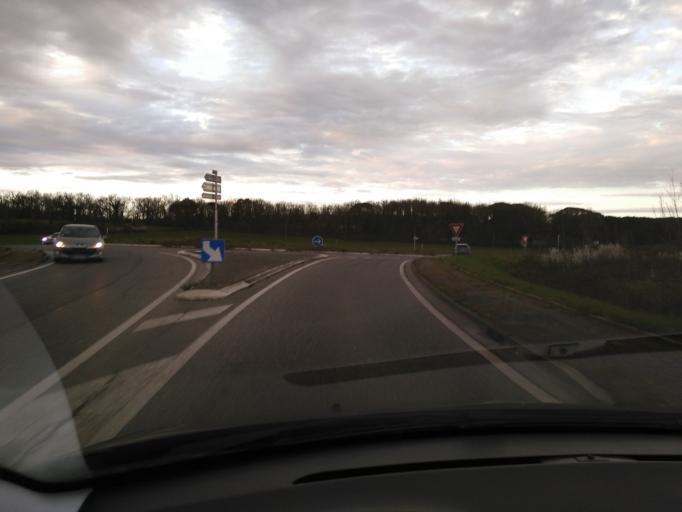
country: FR
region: Midi-Pyrenees
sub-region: Departement de la Haute-Garonne
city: La Salvetat-Saint-Gilles
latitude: 43.5881
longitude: 1.2685
